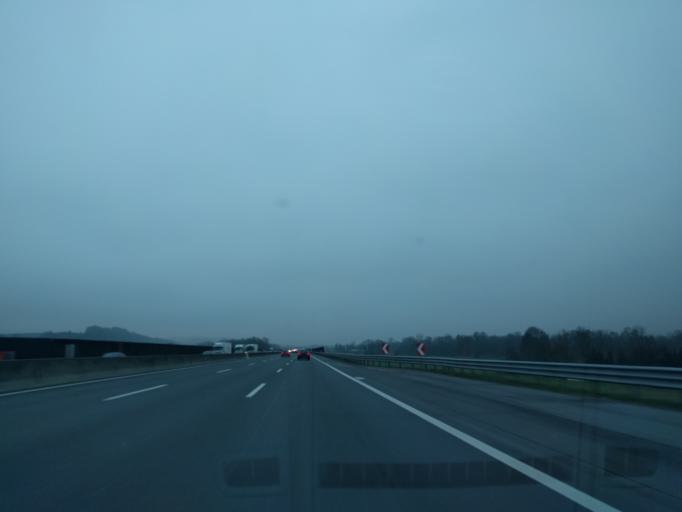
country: AT
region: Lower Austria
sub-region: Politischer Bezirk Melk
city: Ybbs an der Donau
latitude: 48.1454
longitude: 15.0789
